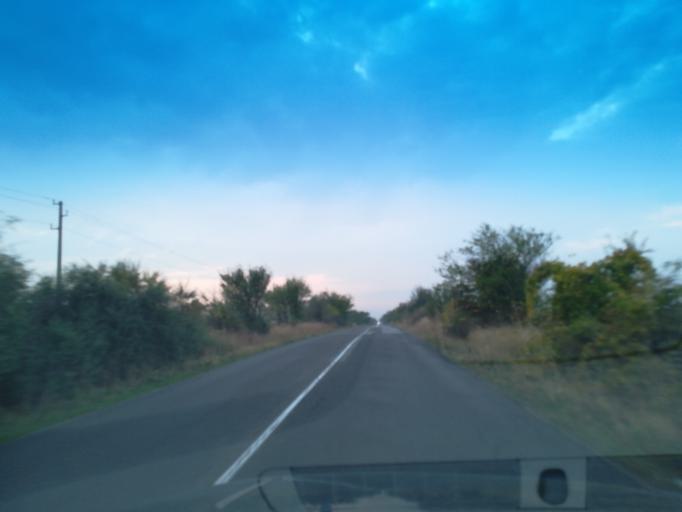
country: BG
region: Stara Zagora
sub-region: Obshtina Chirpan
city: Chirpan
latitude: 42.1928
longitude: 25.2973
